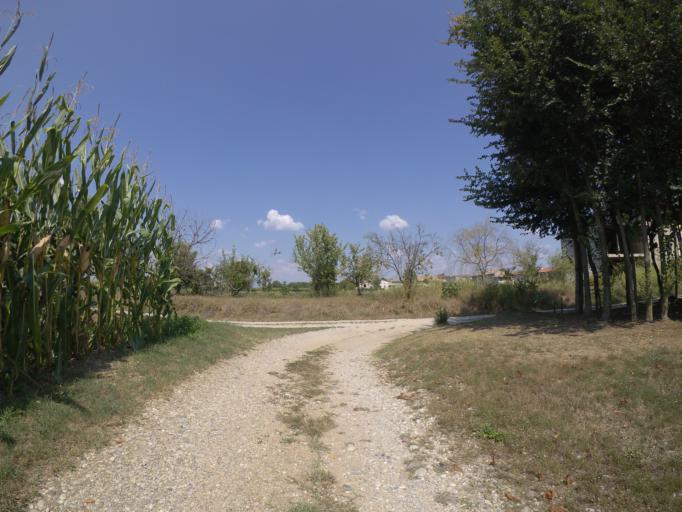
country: IT
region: Friuli Venezia Giulia
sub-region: Provincia di Udine
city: Bertiolo
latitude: 45.9342
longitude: 13.0701
